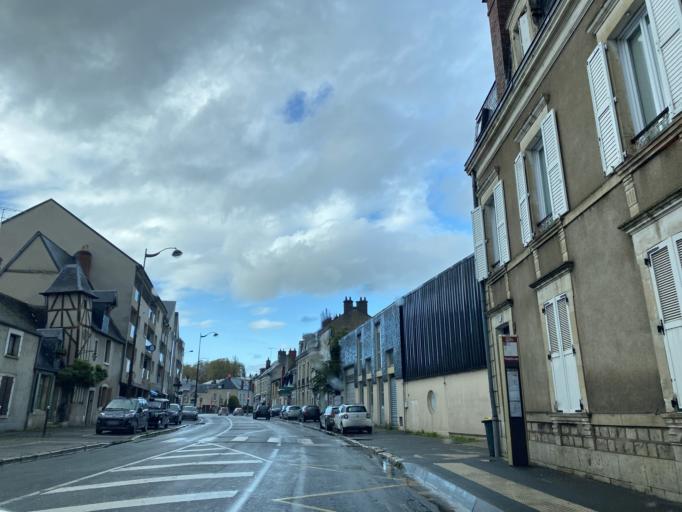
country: FR
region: Centre
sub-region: Departement du Cher
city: Bourges
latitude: 47.0778
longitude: 2.3900
